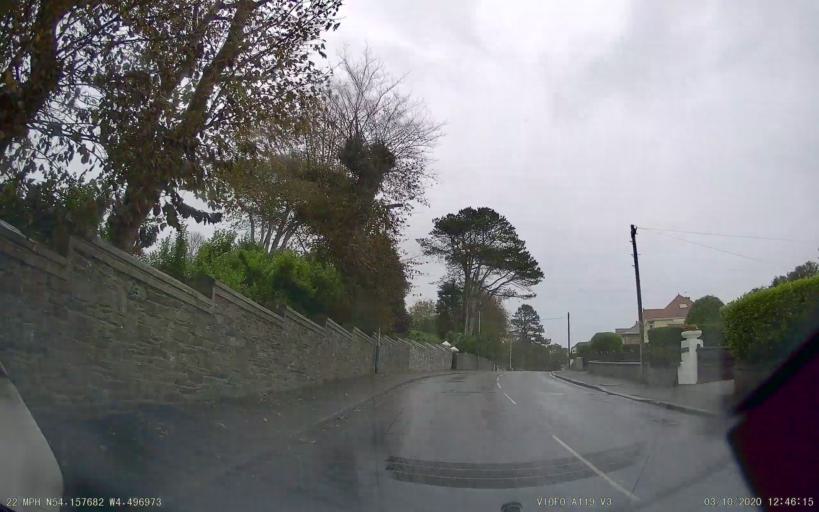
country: IM
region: Douglas
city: Douglas
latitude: 54.1577
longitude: -4.4969
